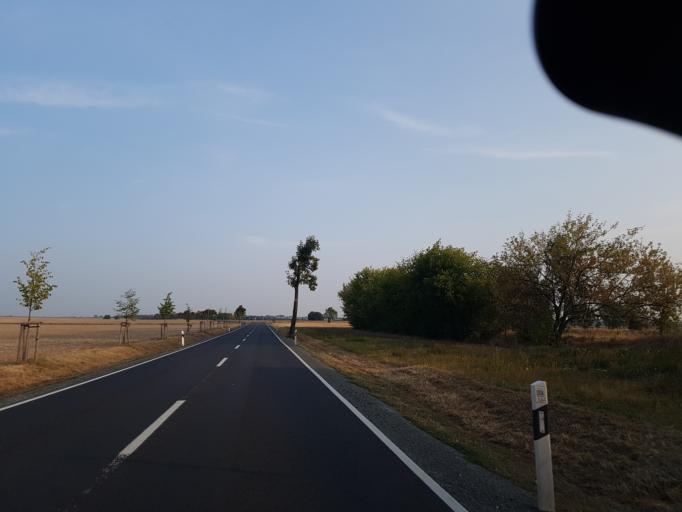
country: DE
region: Saxony
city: Zinna
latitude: 51.5753
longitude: 12.9663
